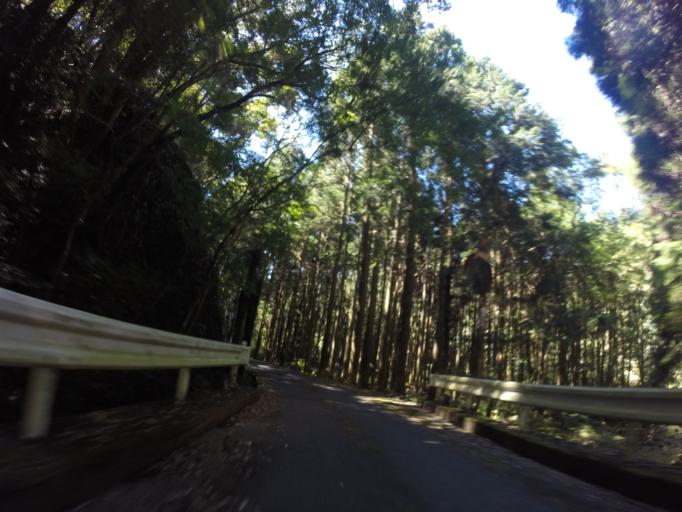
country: JP
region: Shizuoka
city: Kanaya
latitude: 34.8976
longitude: 138.1536
